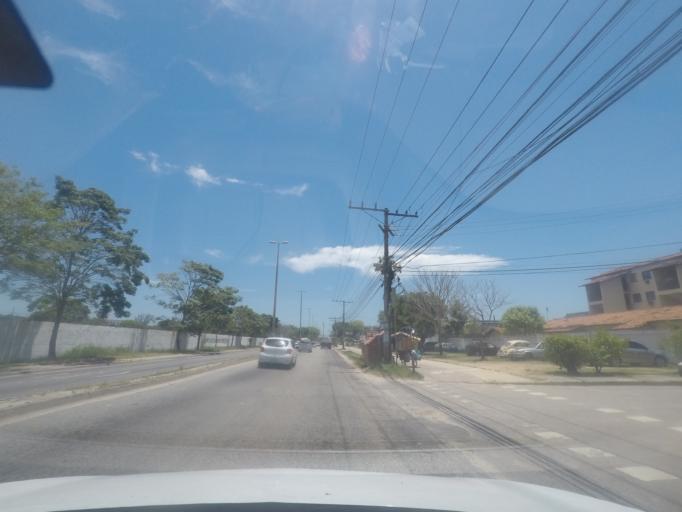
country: BR
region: Rio de Janeiro
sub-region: Itaguai
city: Itaguai
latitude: -22.9069
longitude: -43.6850
